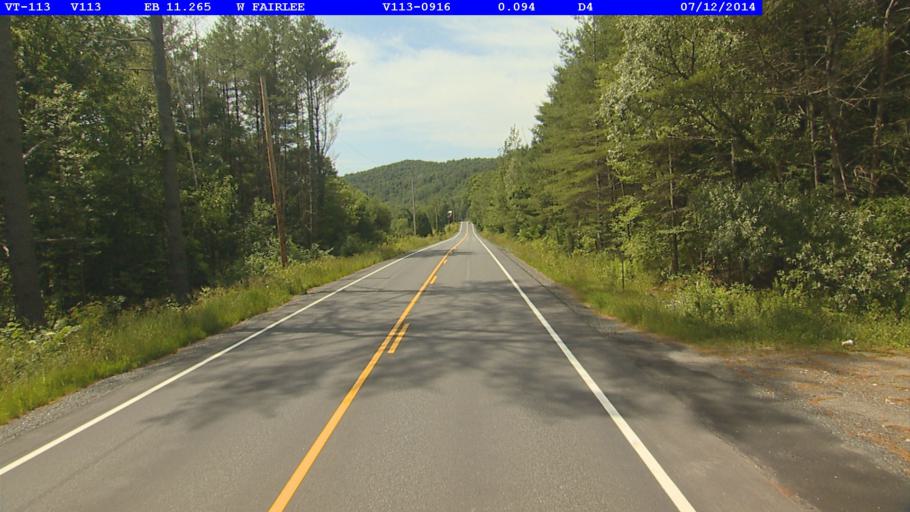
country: US
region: New Hampshire
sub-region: Grafton County
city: Orford
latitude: 43.9350
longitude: -72.2665
